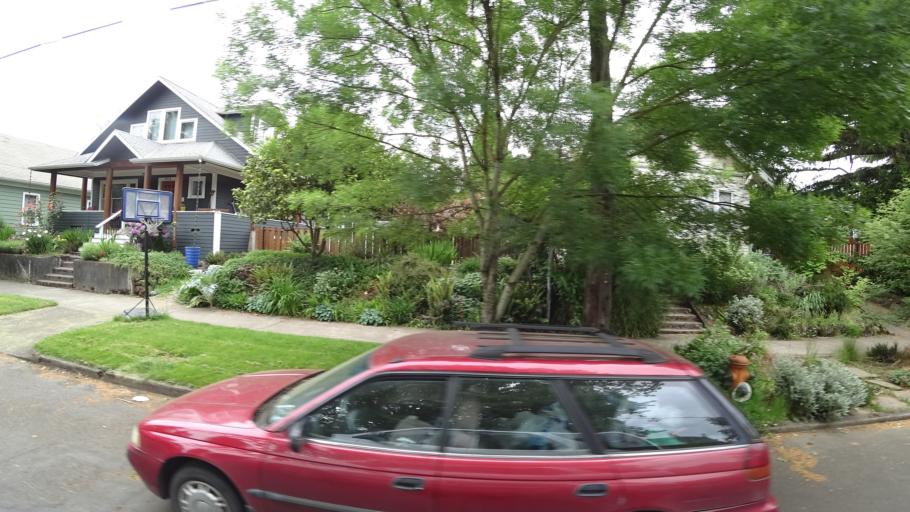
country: US
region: Oregon
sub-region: Multnomah County
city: Portland
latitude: 45.5098
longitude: -122.6213
